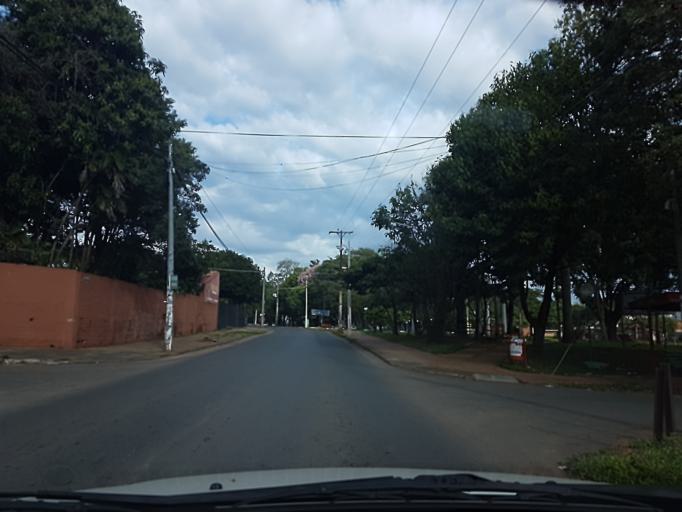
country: PY
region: Central
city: Lambare
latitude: -25.3296
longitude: -57.5804
